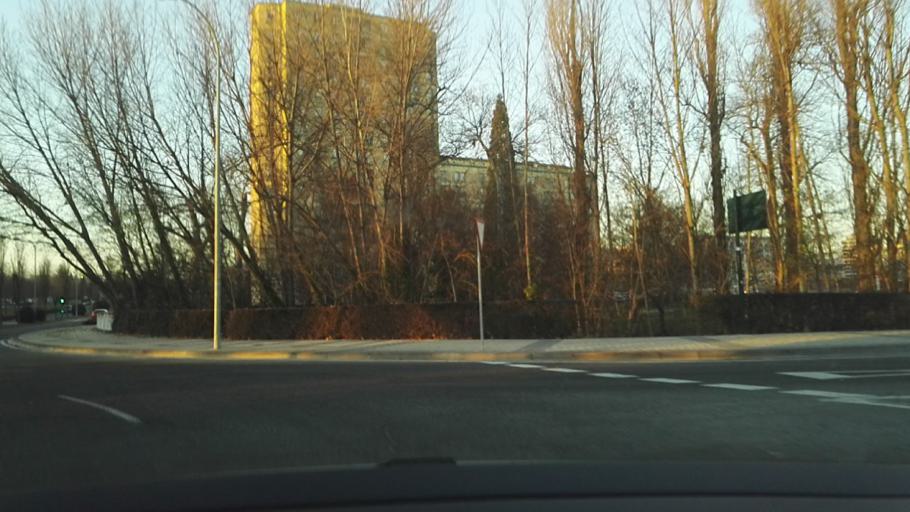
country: ES
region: Navarre
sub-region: Provincia de Navarra
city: Segundo Ensanche
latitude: 42.7967
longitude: -1.6310
